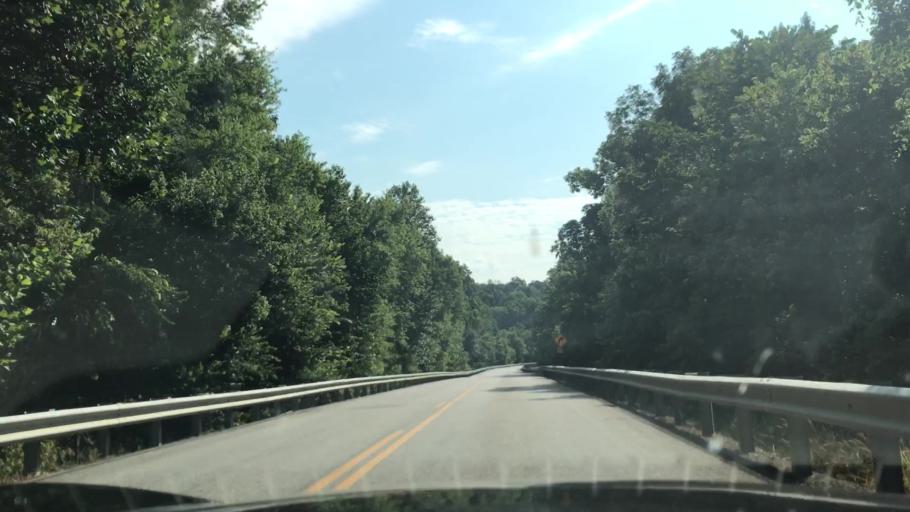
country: US
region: Kentucky
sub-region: Green County
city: Greensburg
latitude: 37.2265
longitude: -85.6768
